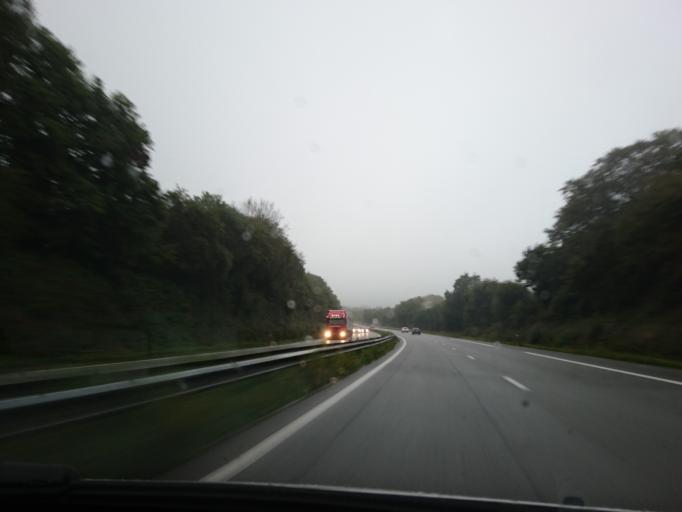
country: FR
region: Brittany
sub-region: Departement du Finistere
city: Landrevarzec
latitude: 48.0485
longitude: -4.0661
